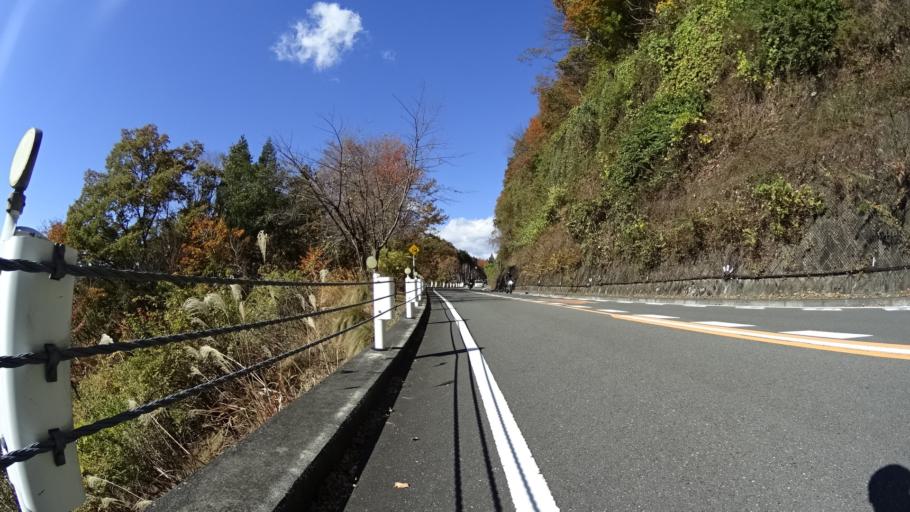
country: JP
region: Yamanashi
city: Uenohara
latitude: 35.7608
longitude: 139.0363
